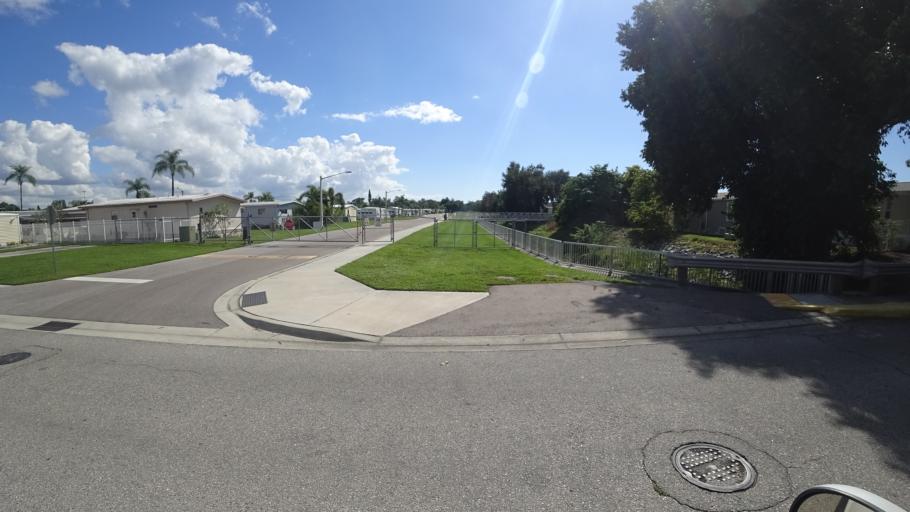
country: US
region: Florida
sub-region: Manatee County
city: South Bradenton
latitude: 27.4809
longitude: -82.5778
